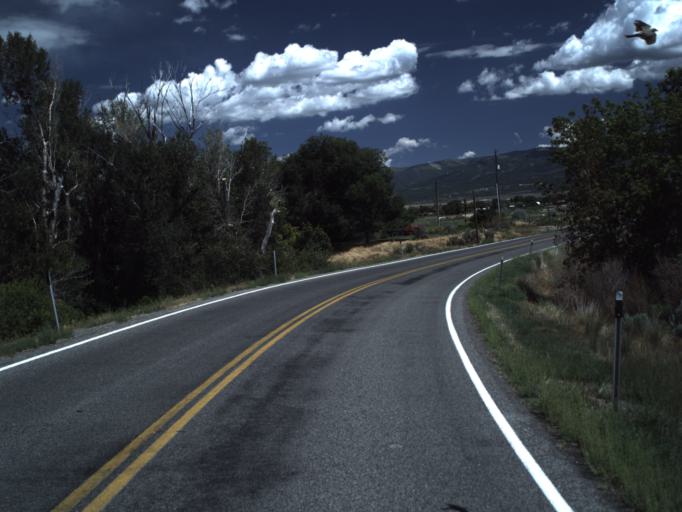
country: US
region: Utah
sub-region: Sanpete County
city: Mount Pleasant
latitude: 39.4816
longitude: -111.5128
